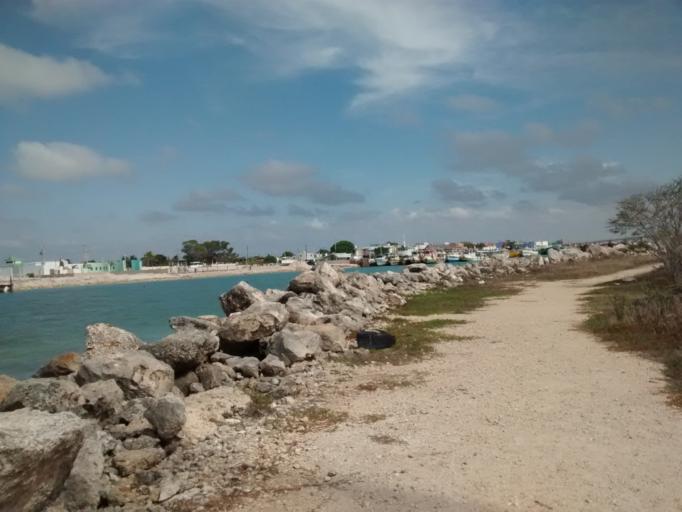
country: MX
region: Yucatan
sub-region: Progreso
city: Chelem
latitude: 21.2796
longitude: -89.7033
